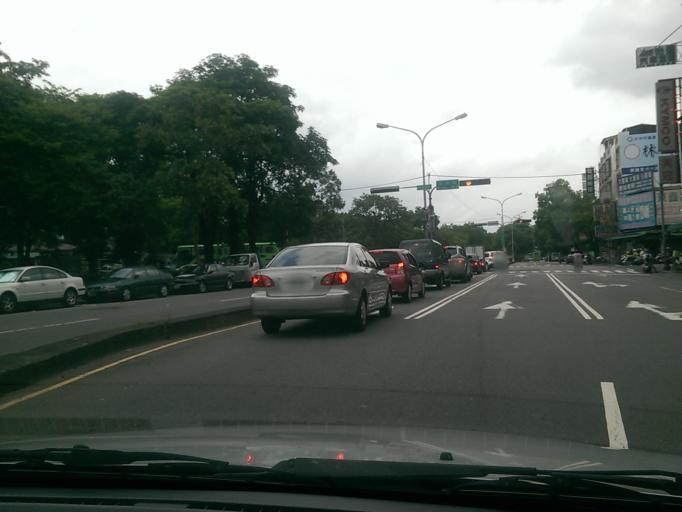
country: TW
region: Taiwan
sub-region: Taichung City
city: Taichung
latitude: 24.1394
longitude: 120.6967
